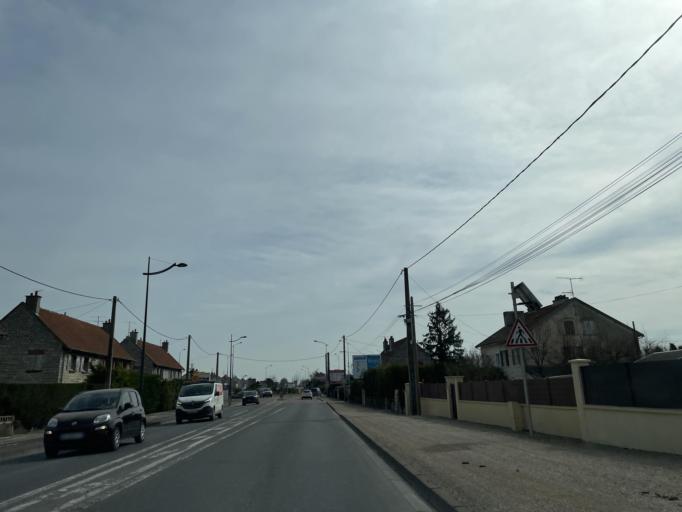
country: FR
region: Champagne-Ardenne
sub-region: Departement de l'Aube
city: Romilly-sur-Seine
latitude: 48.5075
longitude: 3.7432
